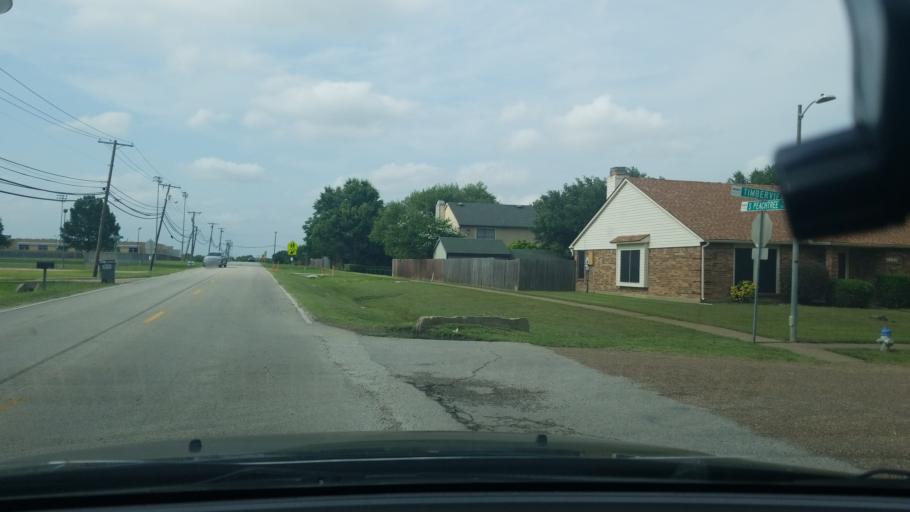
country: US
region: Texas
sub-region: Dallas County
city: Balch Springs
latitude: 32.7591
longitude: -96.6312
